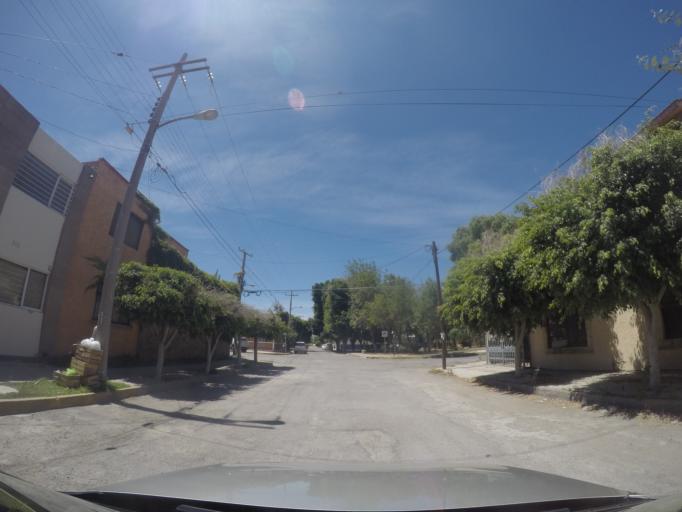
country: MX
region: San Luis Potosi
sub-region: San Luis Potosi
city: San Luis Potosi
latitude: 22.1575
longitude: -100.9873
